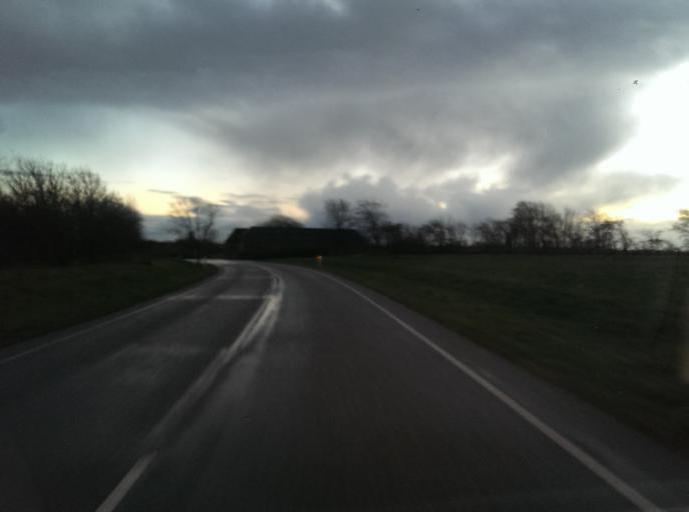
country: DK
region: South Denmark
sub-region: Esbjerg Kommune
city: Bramming
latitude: 55.4570
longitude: 8.6866
